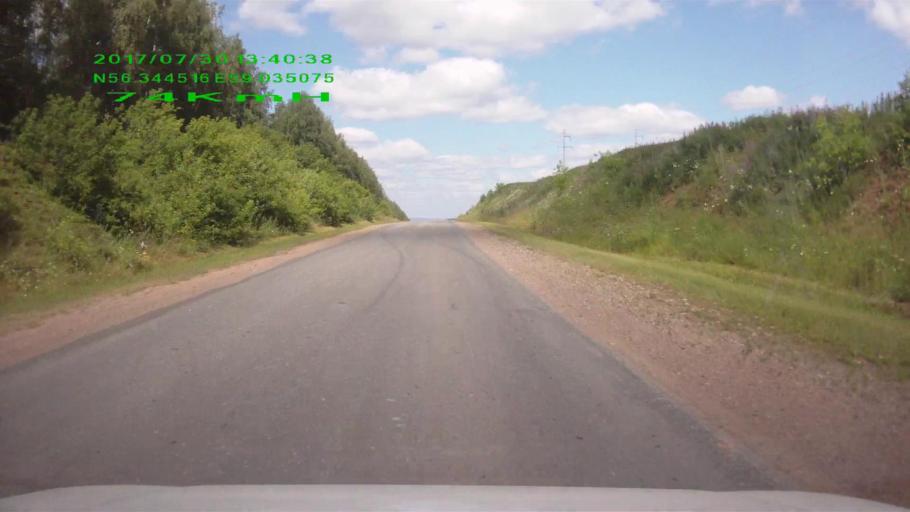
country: RU
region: Sverdlovsk
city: Mikhaylovsk
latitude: 56.3449
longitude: 59.0351
